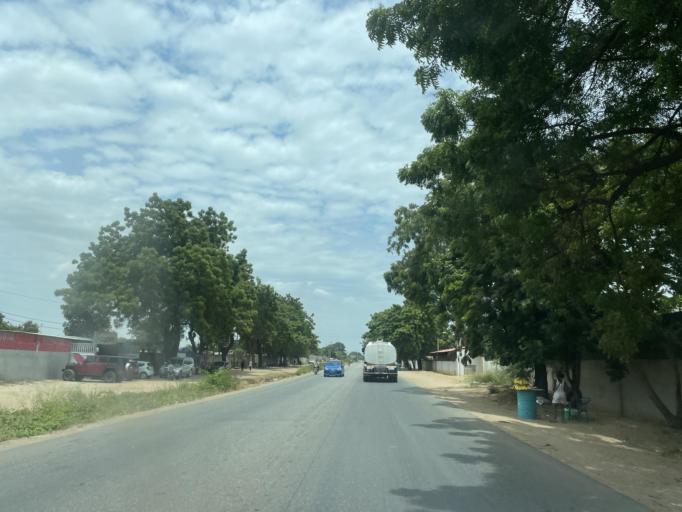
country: AO
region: Luanda
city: Luanda
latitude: -8.9263
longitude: 13.3970
